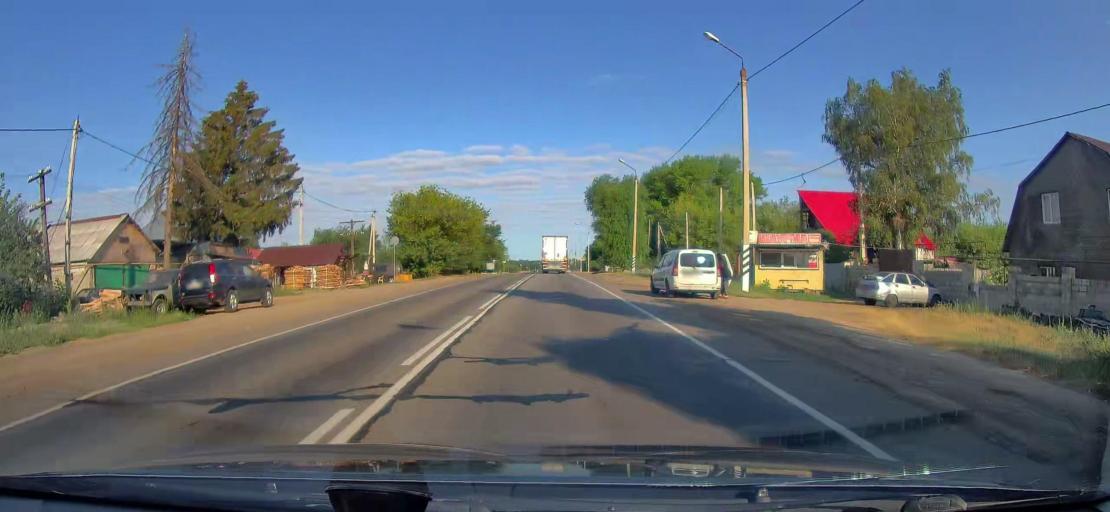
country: RU
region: Tula
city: Chern'
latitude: 53.4532
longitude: 36.8770
